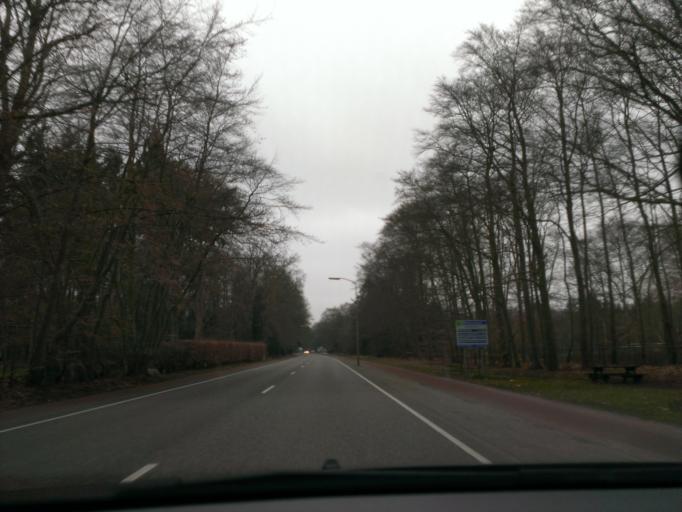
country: NL
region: Gelderland
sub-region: Gemeente Hattem
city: Hattem
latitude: 52.4555
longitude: 6.0674
